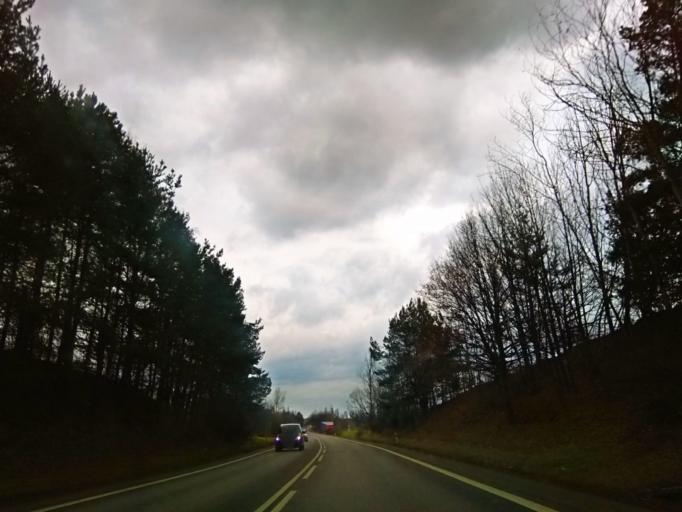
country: CZ
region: Jihocesky
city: Vcelna
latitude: 48.9295
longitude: 14.4477
